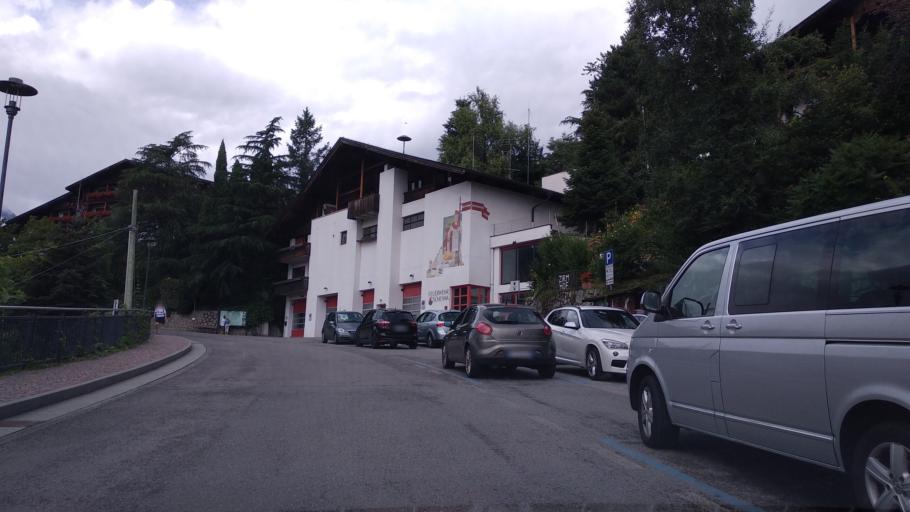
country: IT
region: Trentino-Alto Adige
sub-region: Bolzano
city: Scena
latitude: 46.6875
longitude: 11.1892
